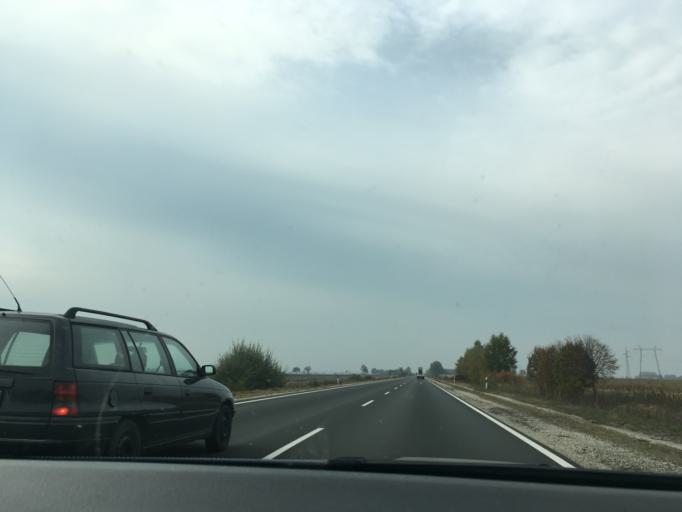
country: HU
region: Pest
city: Abony
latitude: 47.2169
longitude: 20.0359
